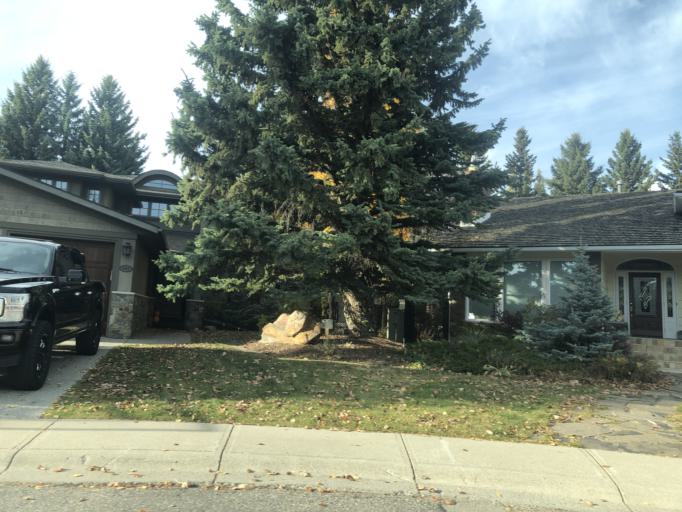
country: CA
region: Alberta
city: Calgary
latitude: 50.9362
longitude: -114.0580
